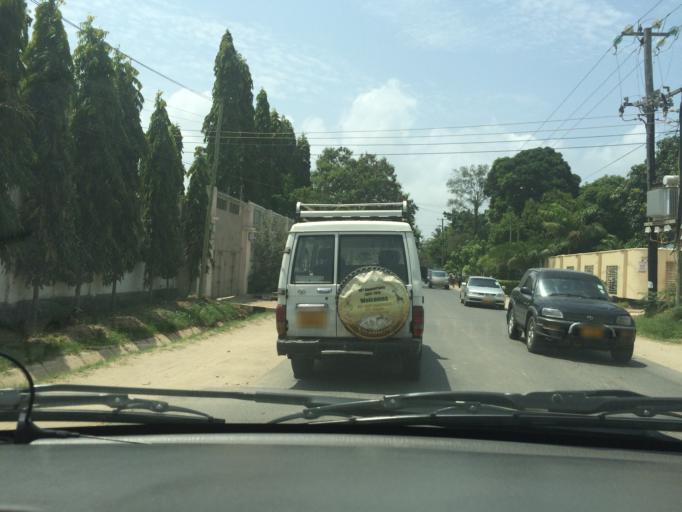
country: TZ
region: Dar es Salaam
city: Magomeni
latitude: -6.7716
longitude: 39.2622
